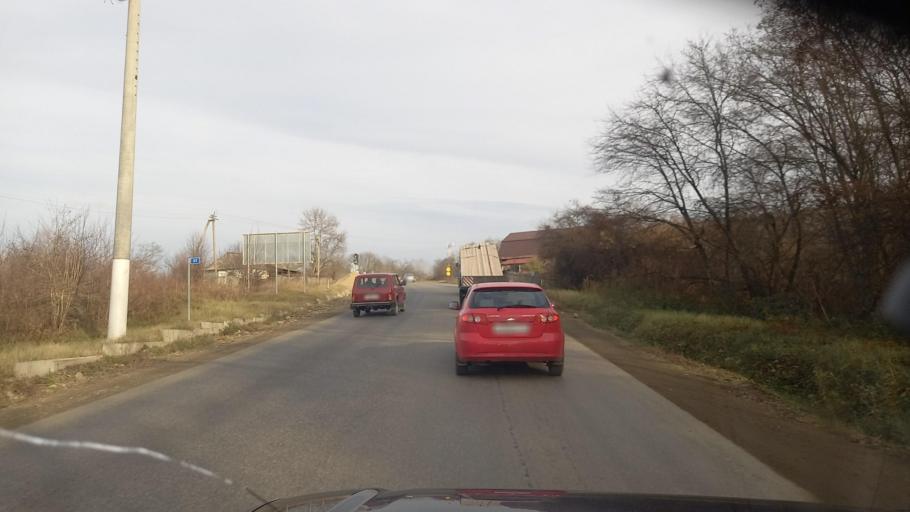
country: RU
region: Krasnodarskiy
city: Apsheronsk
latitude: 44.6040
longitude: 39.6152
